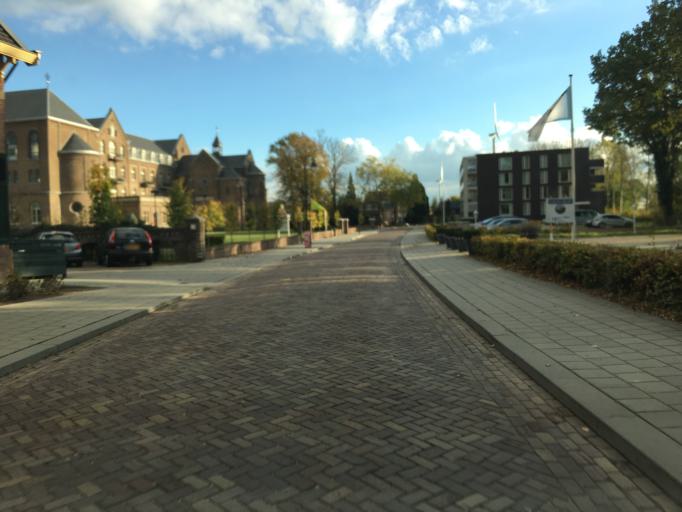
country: NL
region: Gelderland
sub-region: Gemeente Montferland
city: s-Heerenberg
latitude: 51.8729
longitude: 6.2467
